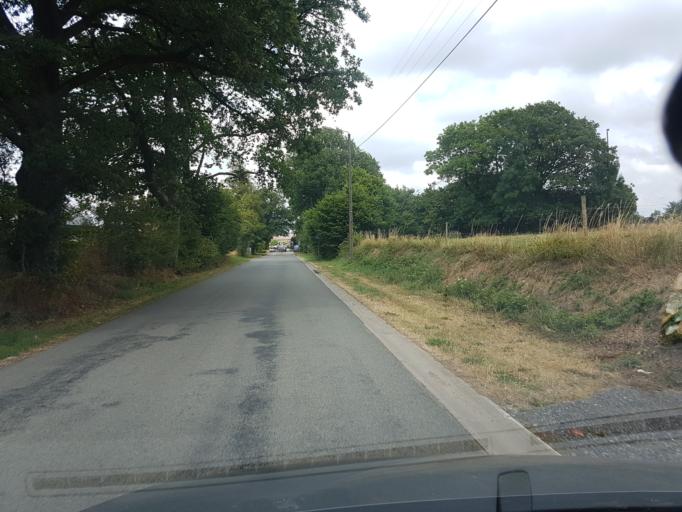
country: BE
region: Wallonia
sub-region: Province du Luxembourg
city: Manhay
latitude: 50.2894
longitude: 5.6734
